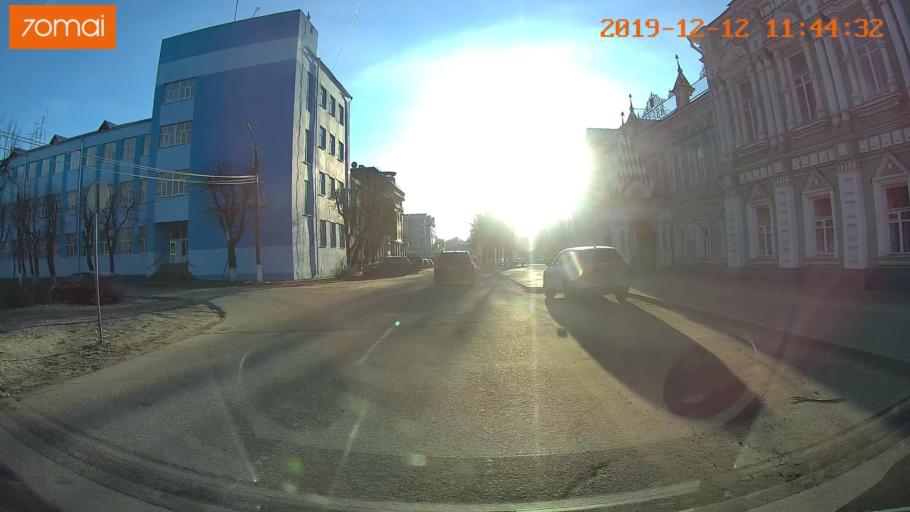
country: RU
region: Ivanovo
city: Shuya
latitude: 56.8544
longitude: 41.3746
